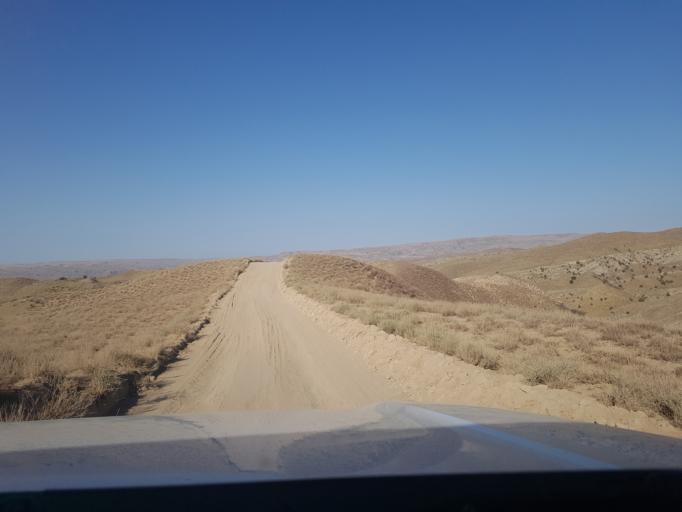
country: TM
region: Balkan
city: Magtymguly
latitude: 38.3038
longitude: 56.8052
